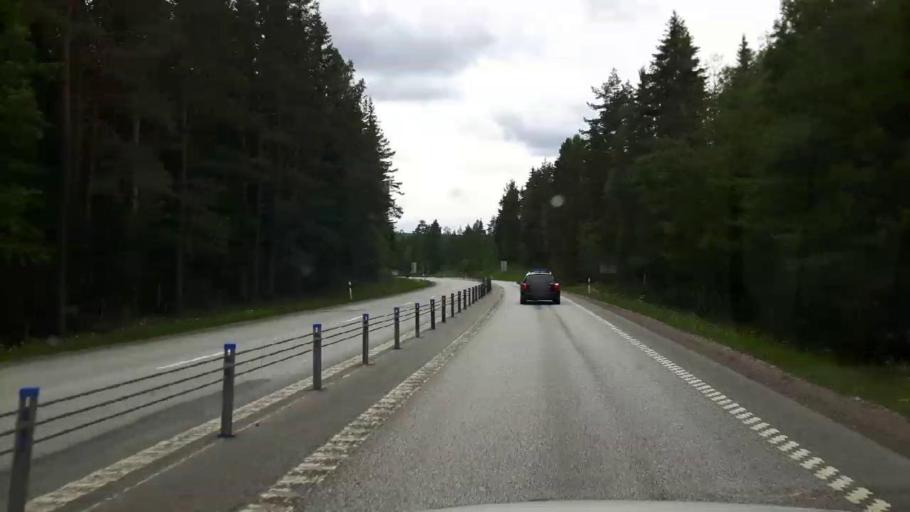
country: SE
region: Vaestmanland
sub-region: Fagersta Kommun
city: Fagersta
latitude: 60.0174
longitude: 15.7849
